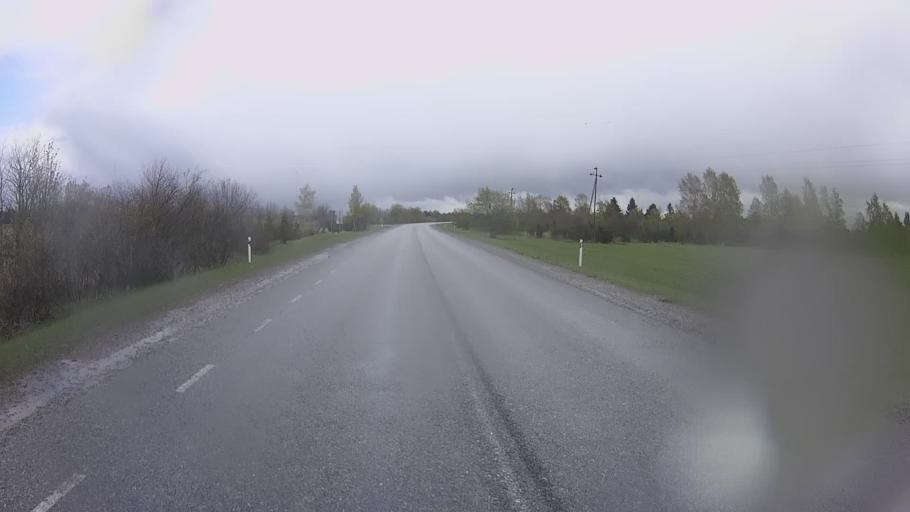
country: EE
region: Hiiumaa
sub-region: Kaerdla linn
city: Kardla
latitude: 58.8331
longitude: 22.7776
